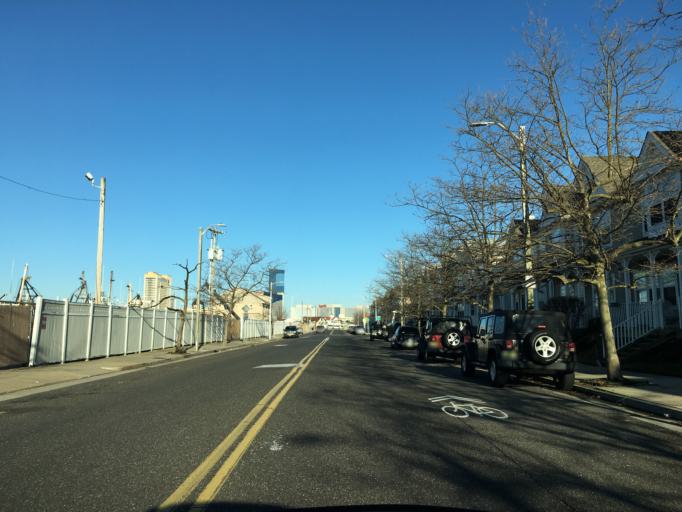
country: US
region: New Jersey
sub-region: Atlantic County
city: Atlantic City
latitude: 39.3732
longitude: -74.4195
